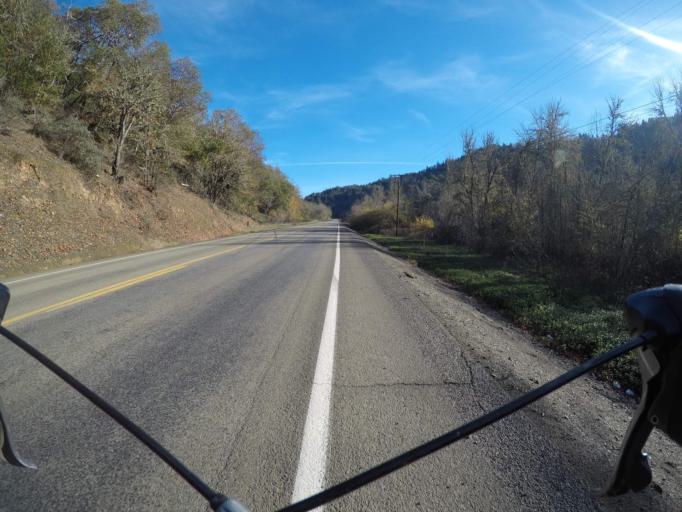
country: US
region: Oregon
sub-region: Douglas County
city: Winston
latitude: 43.1876
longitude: -123.4515
